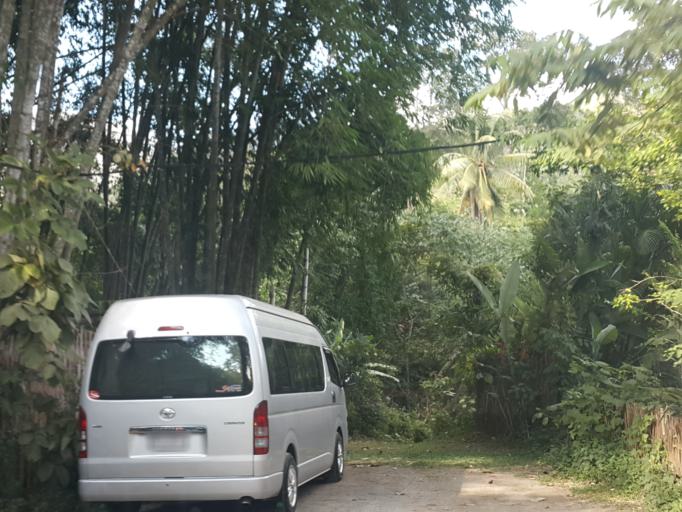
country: TH
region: Chiang Mai
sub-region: Amphoe Chiang Dao
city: Chiang Dao
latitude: 19.4018
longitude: 98.9256
